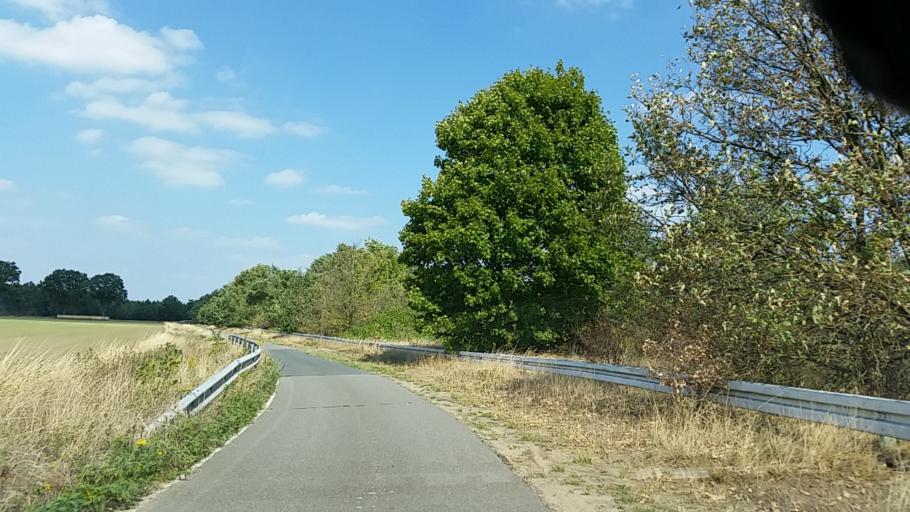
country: DE
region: Lower Saxony
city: Wendisch Evern
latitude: 53.2223
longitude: 10.4911
